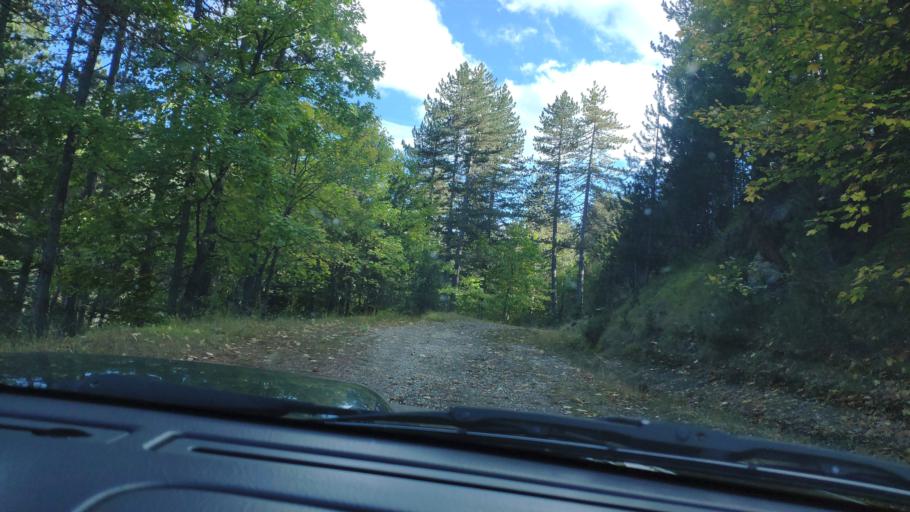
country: AL
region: Korce
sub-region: Rrethi i Devollit
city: Miras
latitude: 40.3848
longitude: 20.8859
